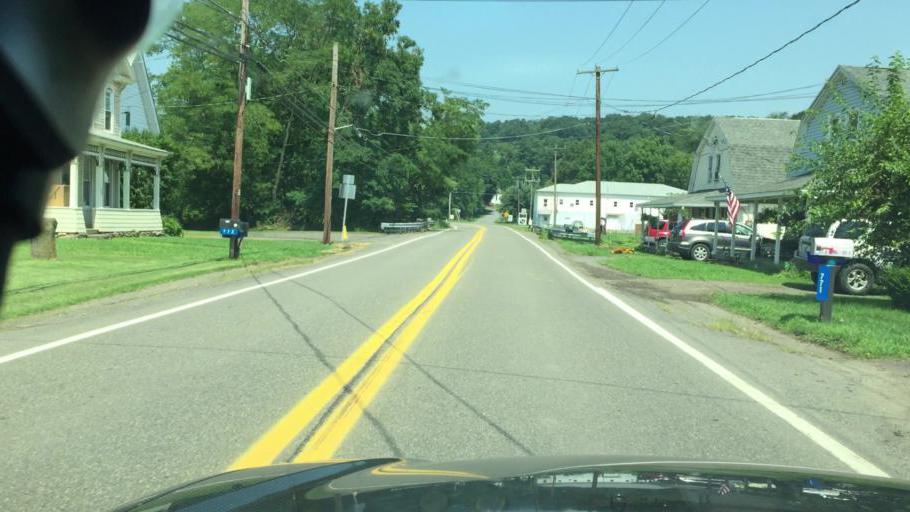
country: US
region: Pennsylvania
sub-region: Columbia County
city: Almedia
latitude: 40.9772
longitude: -76.3742
